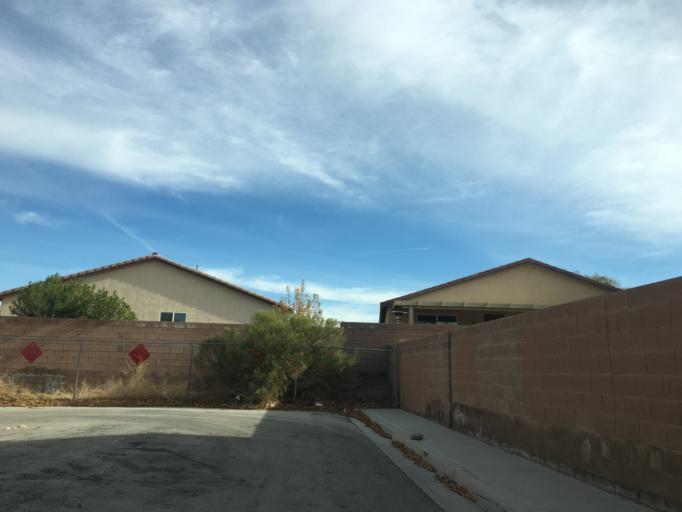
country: US
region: Nevada
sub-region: Clark County
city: Enterprise
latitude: 36.0160
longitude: -115.1659
